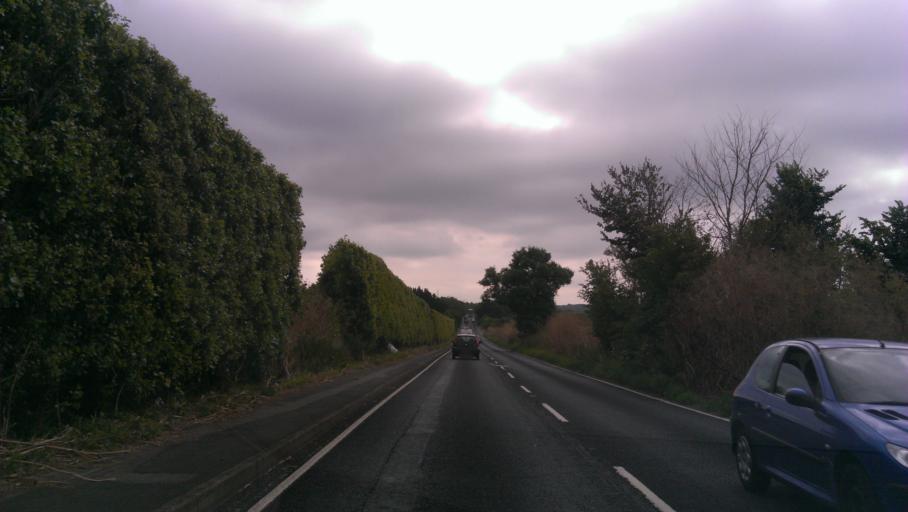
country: GB
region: England
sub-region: Kent
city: Faversham
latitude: 51.3039
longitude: 0.9132
